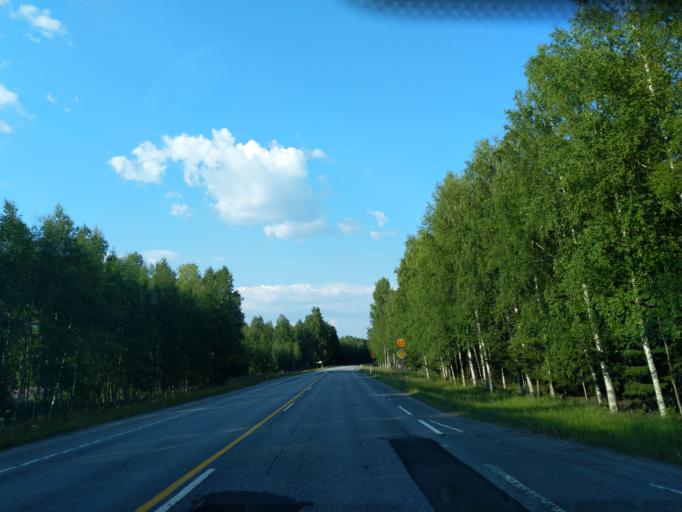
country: FI
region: Satakunta
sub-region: Pori
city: Laengelmaeki
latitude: 61.7446
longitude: 22.0975
